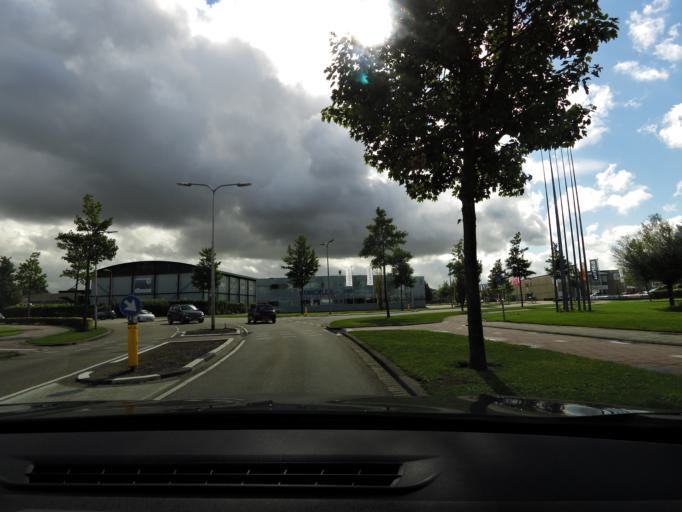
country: NL
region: South Holland
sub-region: Gemeente Oud-Beijerland
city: Oud-Beijerland
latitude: 51.8258
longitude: 4.4395
